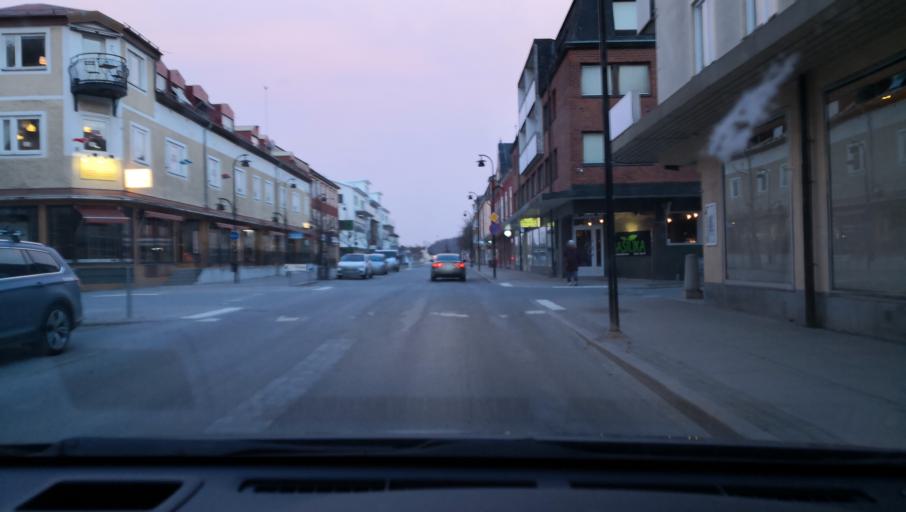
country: SE
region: OErebro
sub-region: Lindesbergs Kommun
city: Lindesberg
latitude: 59.5933
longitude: 15.2278
